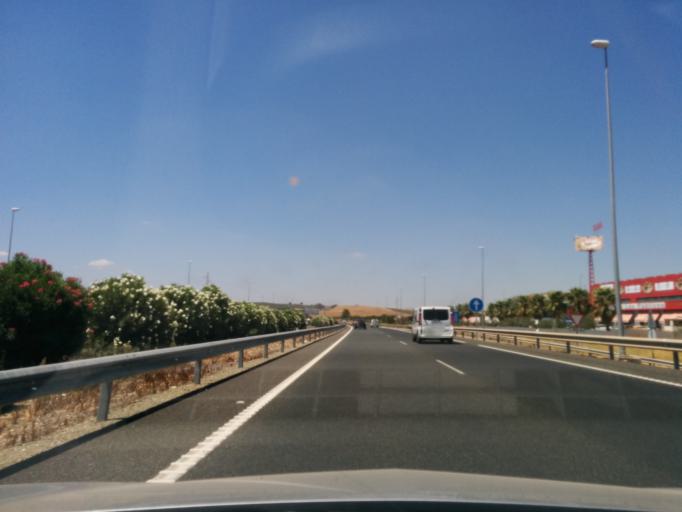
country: ES
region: Andalusia
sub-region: Provincia de Sevilla
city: Carrion de los Cespedes
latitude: 37.3593
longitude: -6.3260
